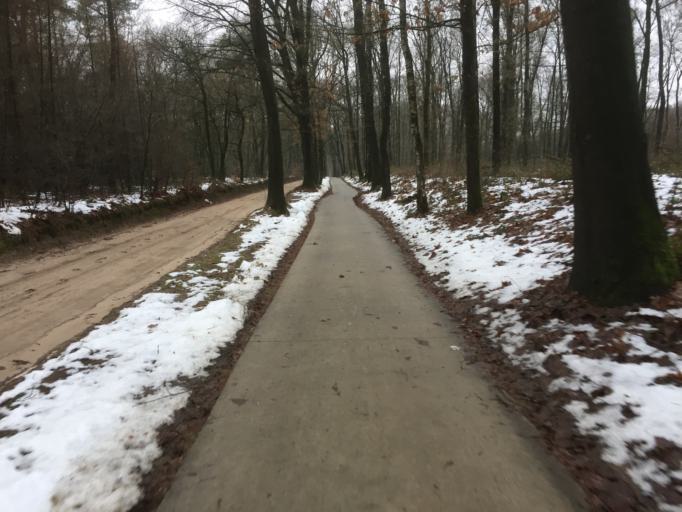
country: NL
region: Gelderland
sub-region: Gemeente Ede
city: Bennekom
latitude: 52.0202
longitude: 5.7100
